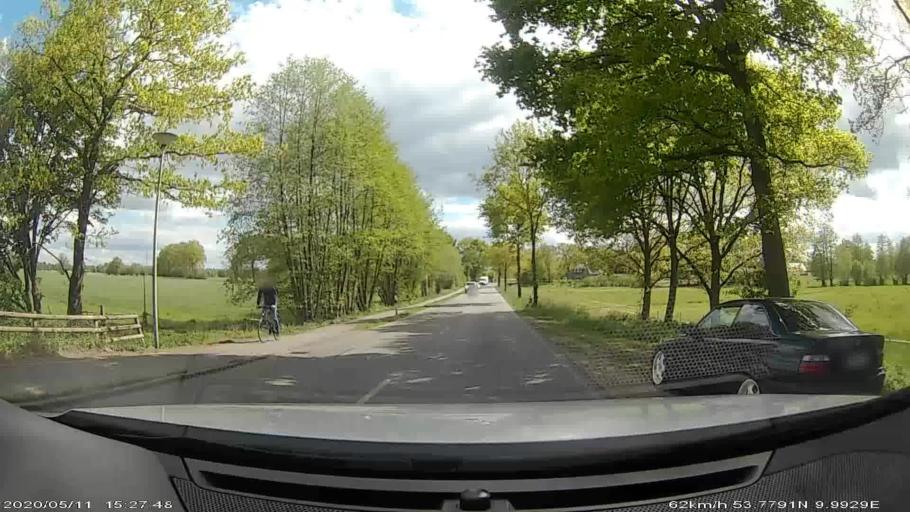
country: DE
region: Schleswig-Holstein
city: Henstedt-Ulzburg
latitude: 53.7673
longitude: 9.9947
